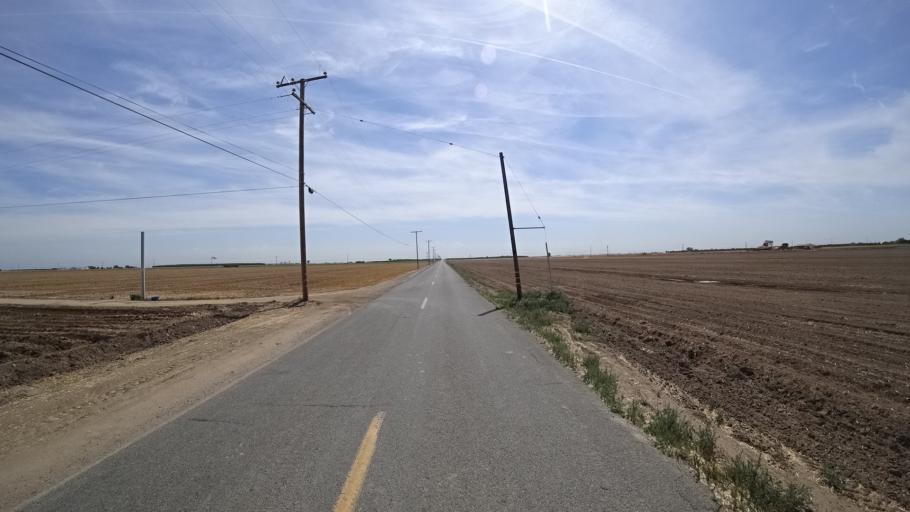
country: US
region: California
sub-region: Kings County
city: Hanford
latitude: 36.3574
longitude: -119.5699
